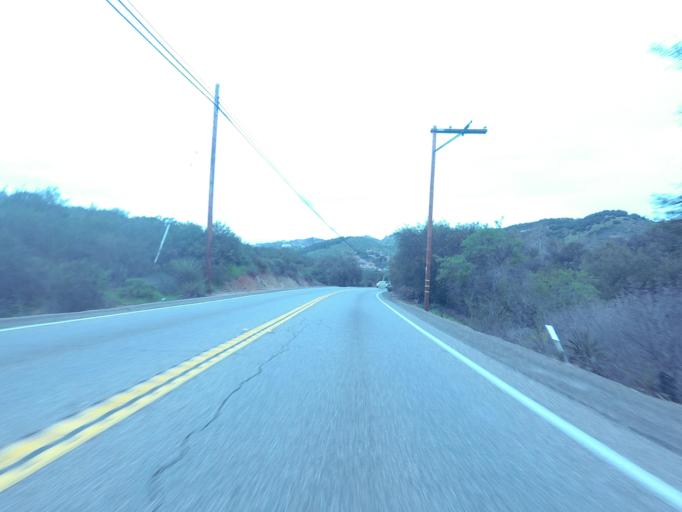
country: US
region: California
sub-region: San Diego County
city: Bonsall
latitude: 33.2555
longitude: -117.2148
